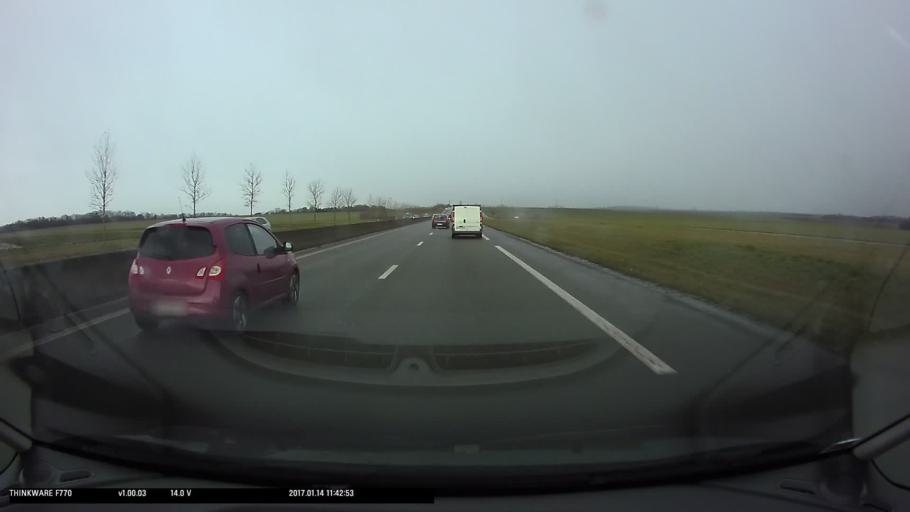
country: FR
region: Ile-de-France
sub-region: Departement du Val-d'Oise
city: Sagy
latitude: 49.0739
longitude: 1.9529
